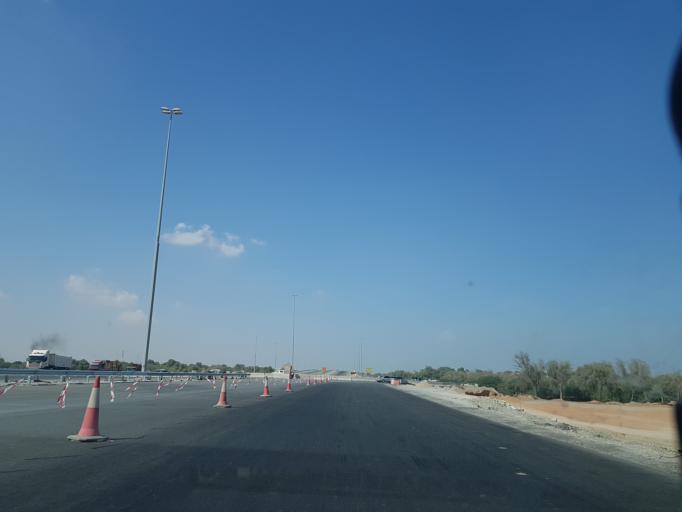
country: AE
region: Ra's al Khaymah
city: Ras al-Khaimah
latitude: 25.6982
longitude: 55.9739
